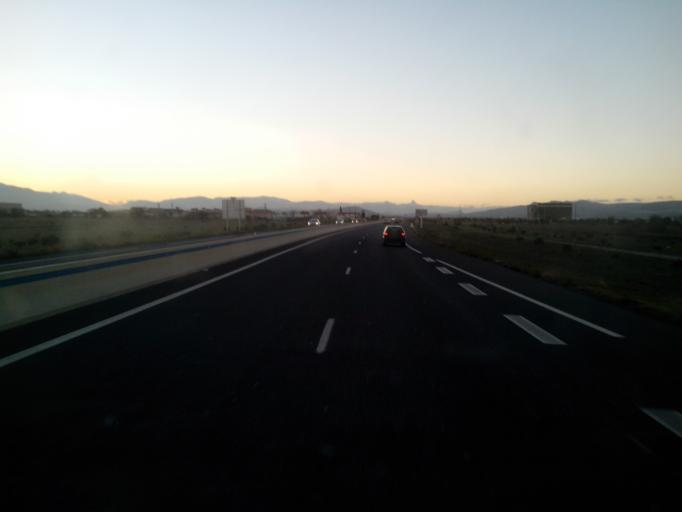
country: FR
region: Languedoc-Roussillon
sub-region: Departement des Pyrenees-Orientales
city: Saint-Hippolyte
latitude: 42.7774
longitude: 2.9567
